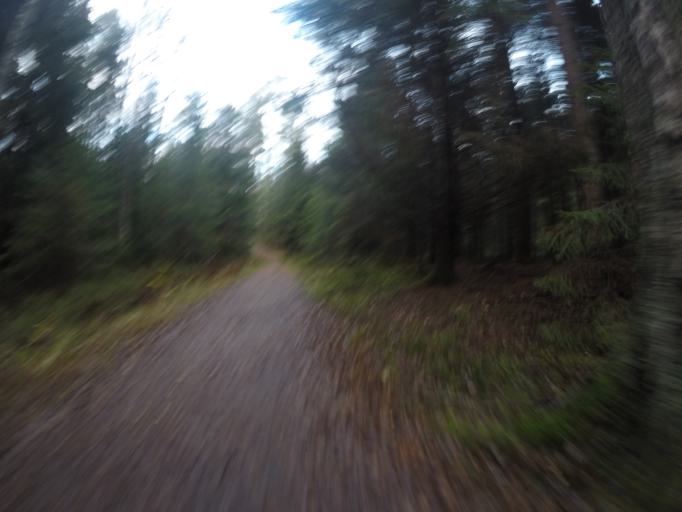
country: SE
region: Soedermanland
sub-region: Eskilstuna Kommun
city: Eskilstuna
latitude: 59.3396
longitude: 16.5206
